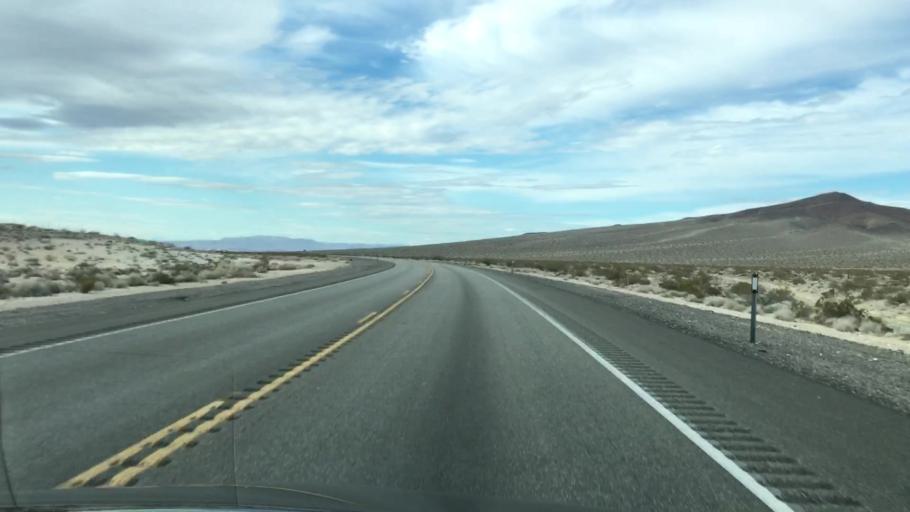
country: US
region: Nevada
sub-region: Nye County
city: Beatty
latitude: 36.6310
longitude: -116.3185
